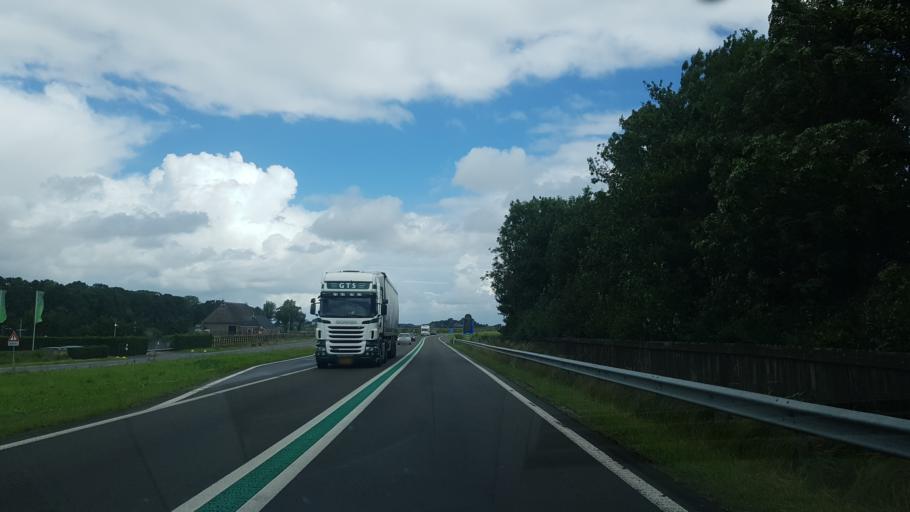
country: NL
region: Friesland
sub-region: Gemeente Dongeradeel
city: Dokkum
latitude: 53.3263
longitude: 6.0225
